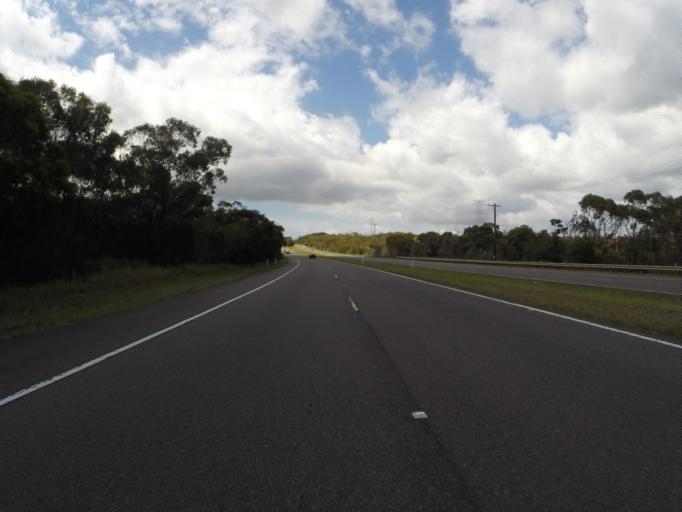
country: AU
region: New South Wales
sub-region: Sutherland Shire
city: Heathcote
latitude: -34.1143
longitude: 150.9920
